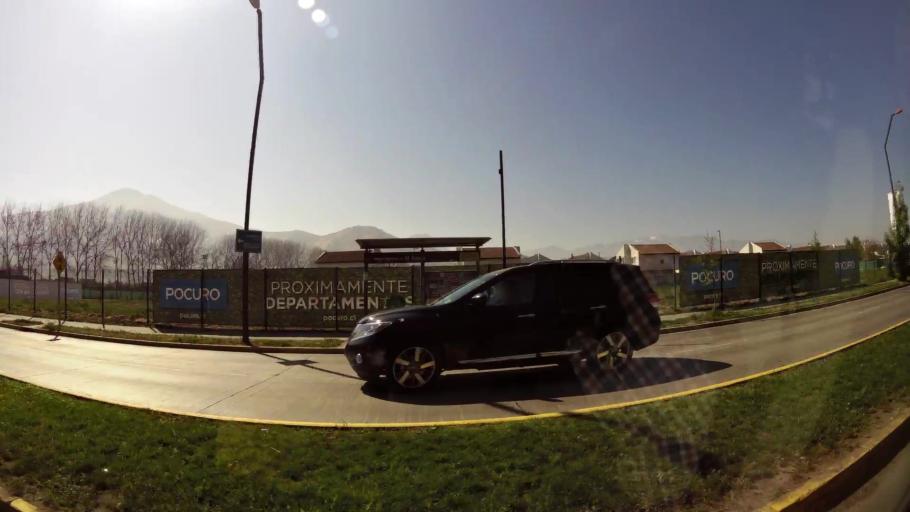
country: CL
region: Santiago Metropolitan
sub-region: Provincia de Chacabuco
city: Chicureo Abajo
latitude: -33.3624
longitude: -70.6706
